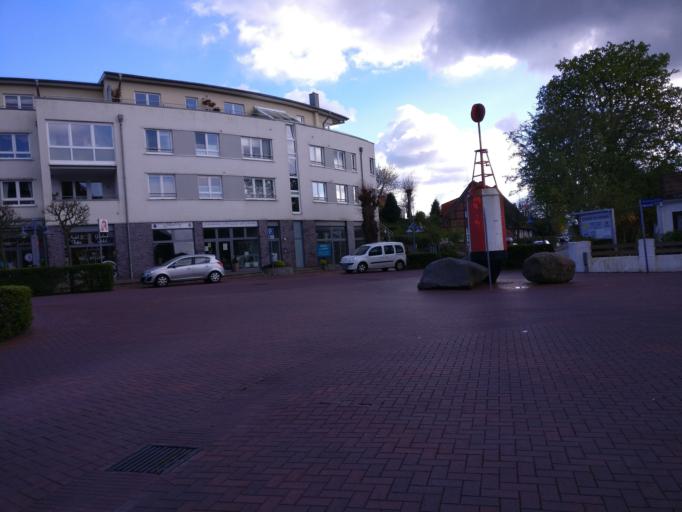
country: DE
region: Schleswig-Holstein
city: Laboe
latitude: 54.4044
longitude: 10.2216
